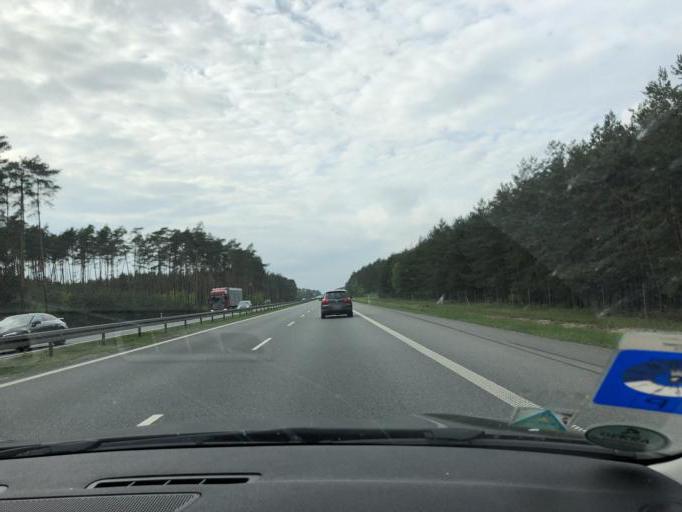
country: PL
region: Opole Voivodeship
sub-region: Powiat opolski
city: Komprachcice
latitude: 50.6089
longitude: 17.7803
